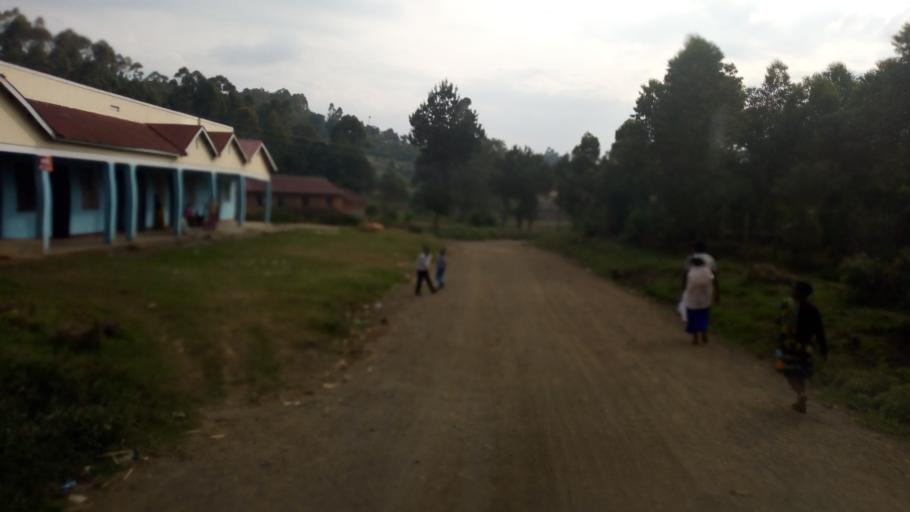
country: UG
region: Western Region
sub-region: Kisoro District
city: Kisoro
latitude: -1.2911
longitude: 29.6939
